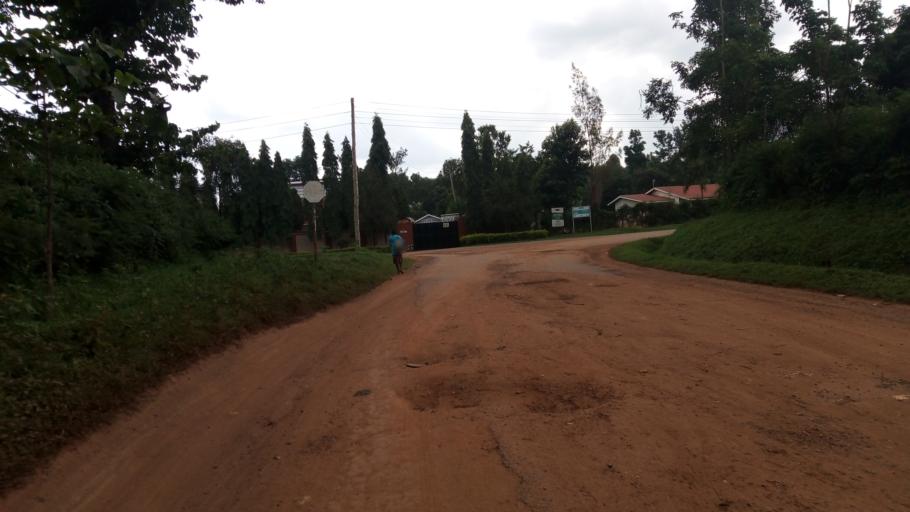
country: UG
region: Eastern Region
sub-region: Mbale District
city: Mbale
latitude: 1.0718
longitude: 34.1924
